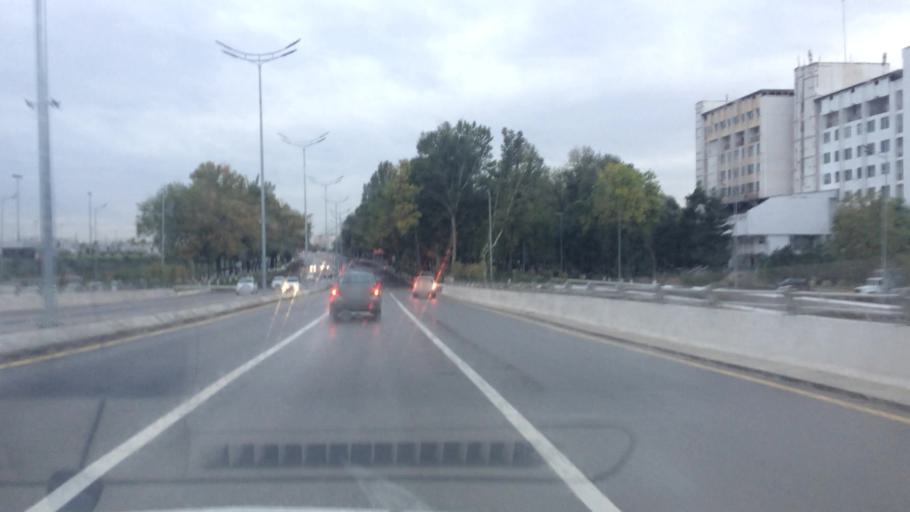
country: UZ
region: Toshkent Shahri
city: Tashkent
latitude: 41.2801
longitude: 69.2099
